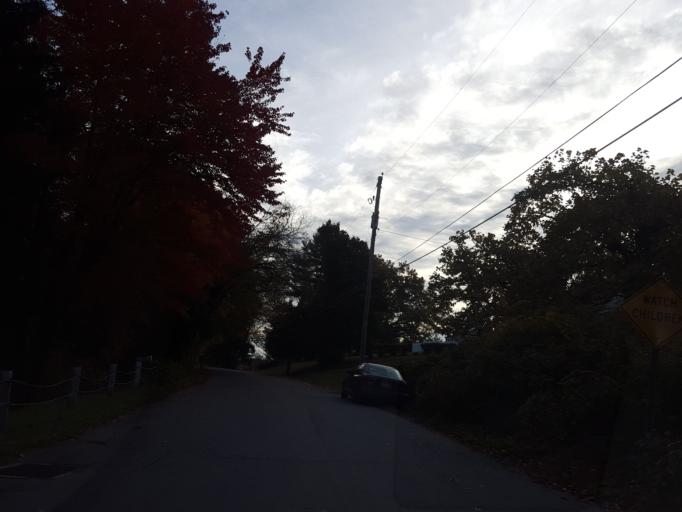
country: US
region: Pennsylvania
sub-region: York County
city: Stonybrook
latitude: 39.9764
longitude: -76.6332
